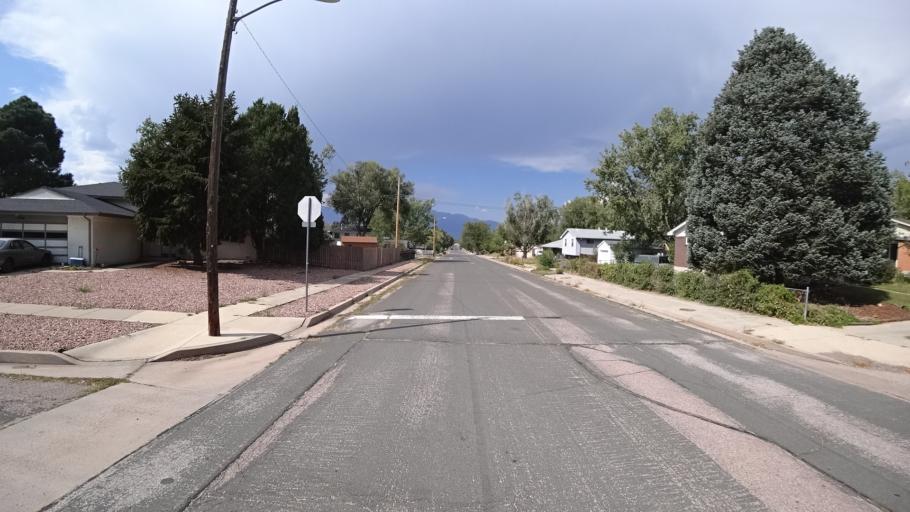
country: US
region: Colorado
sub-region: El Paso County
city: Cimarron Hills
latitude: 38.8617
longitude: -104.7619
